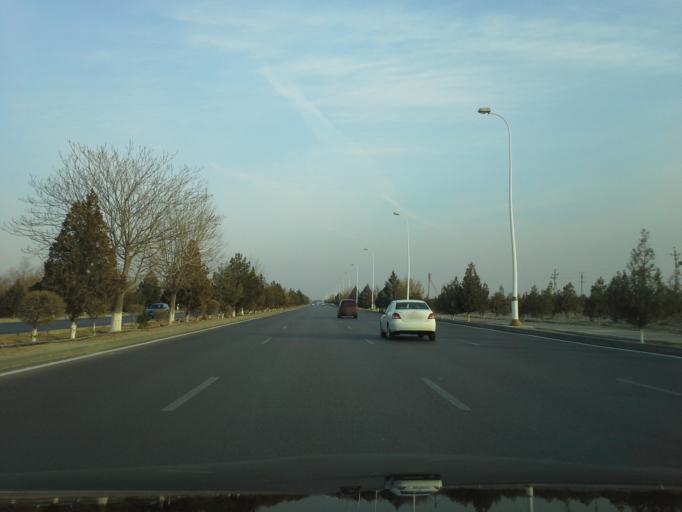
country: TM
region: Ahal
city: Abadan
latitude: 38.0395
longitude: 58.2130
